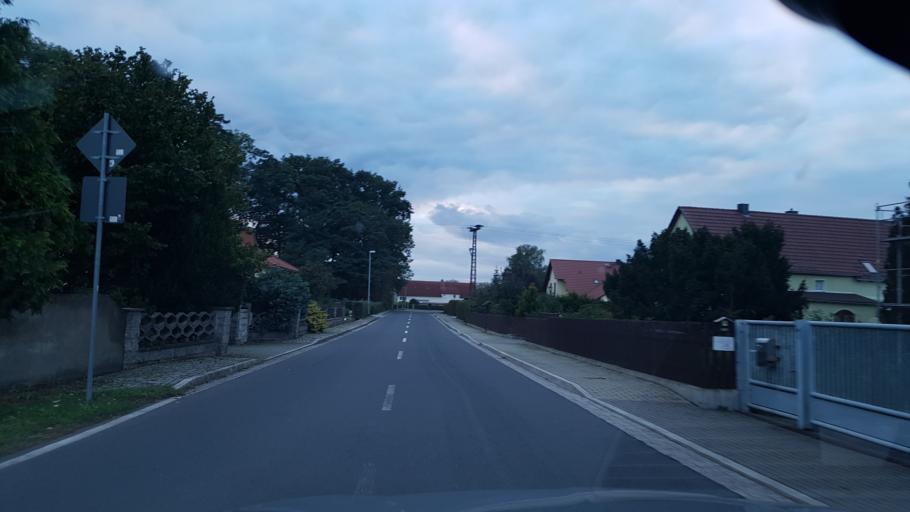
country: DE
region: Saxony
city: Grossenhain
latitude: 51.3190
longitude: 13.5869
